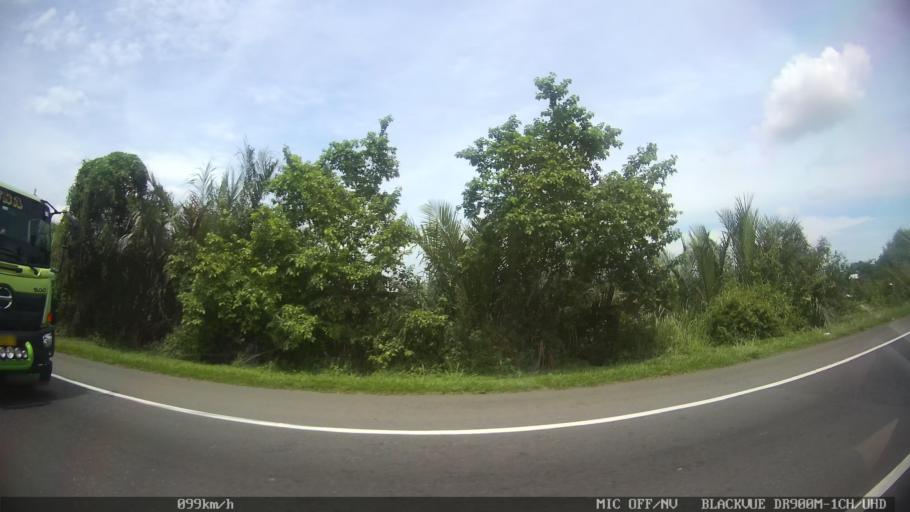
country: ID
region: North Sumatra
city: Belawan
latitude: 3.7551
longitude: 98.6824
